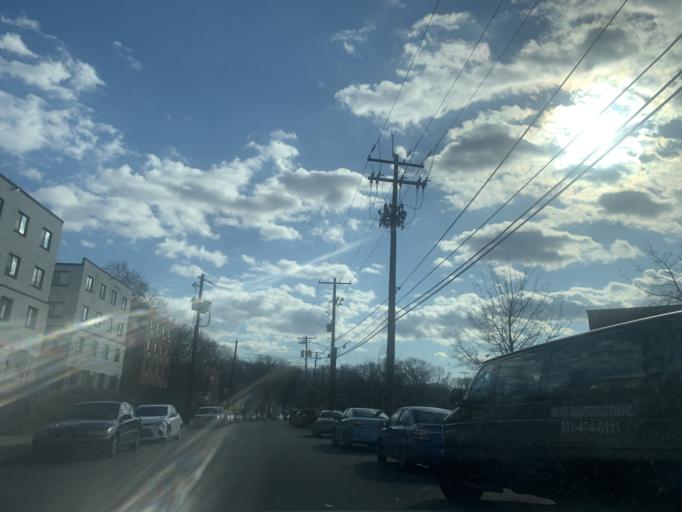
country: US
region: Maryland
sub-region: Prince George's County
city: Coral Hills
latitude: 38.8848
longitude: -76.9525
